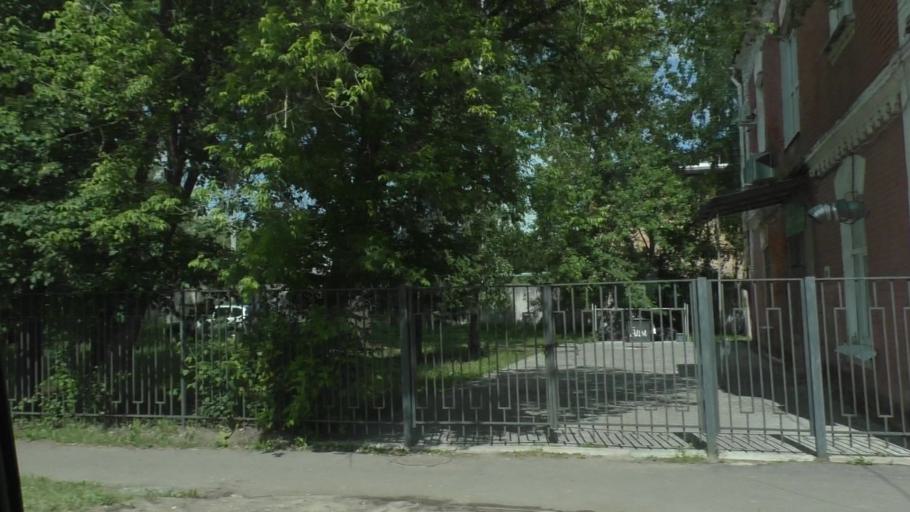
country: RU
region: Moskovskaya
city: Yegor'yevsk
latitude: 55.3844
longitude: 39.0374
